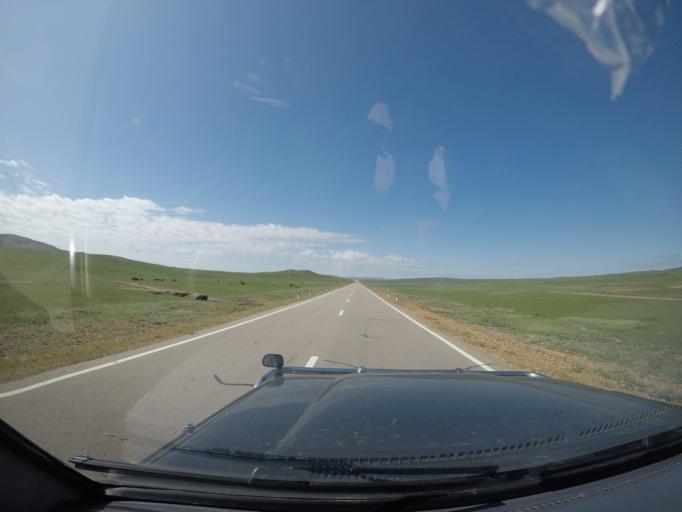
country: MN
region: Suhbaatar
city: Hanhohiy
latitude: 47.4919
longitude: 111.9800
